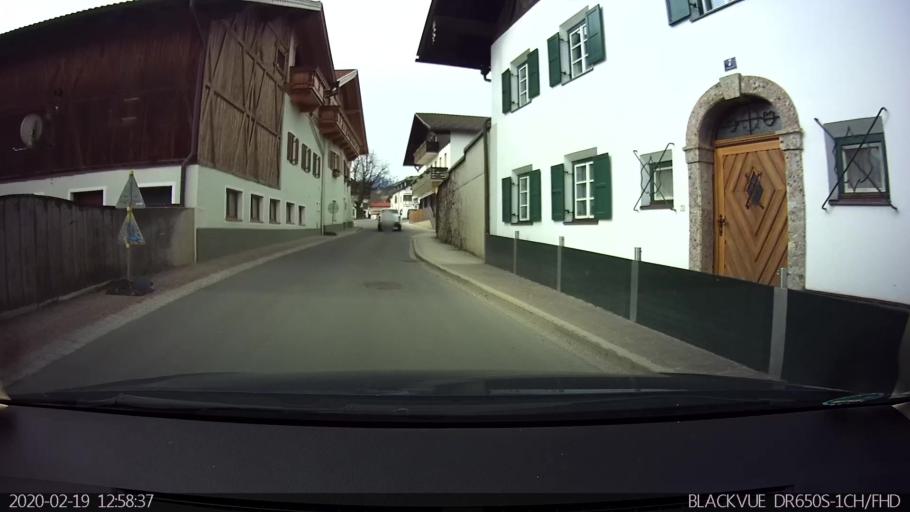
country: AT
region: Tyrol
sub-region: Politischer Bezirk Innsbruck Land
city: Thaur
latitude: 47.2938
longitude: 11.4745
